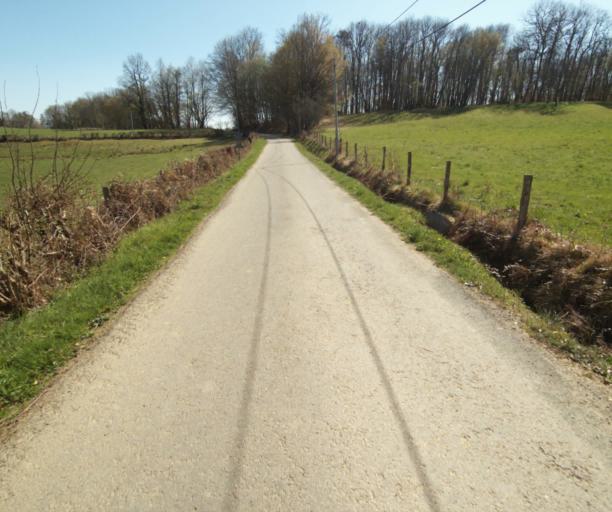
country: FR
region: Limousin
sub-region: Departement de la Correze
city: Chameyrat
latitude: 45.2530
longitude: 1.7064
